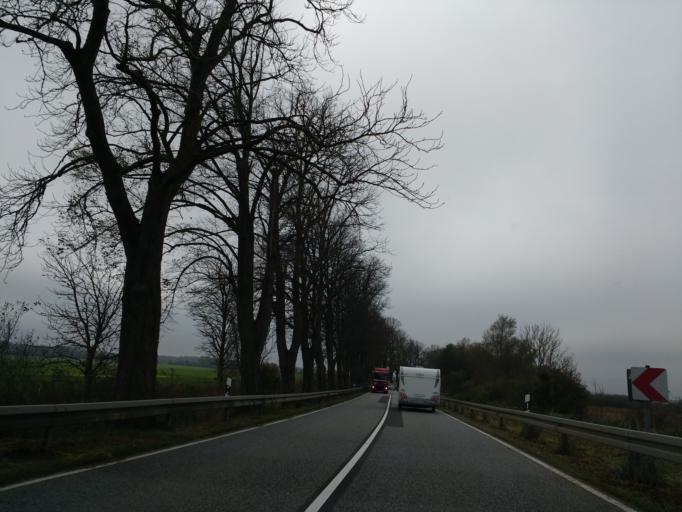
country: DE
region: Mecklenburg-Vorpommern
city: Dassow
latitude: 53.9043
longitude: 10.9511
